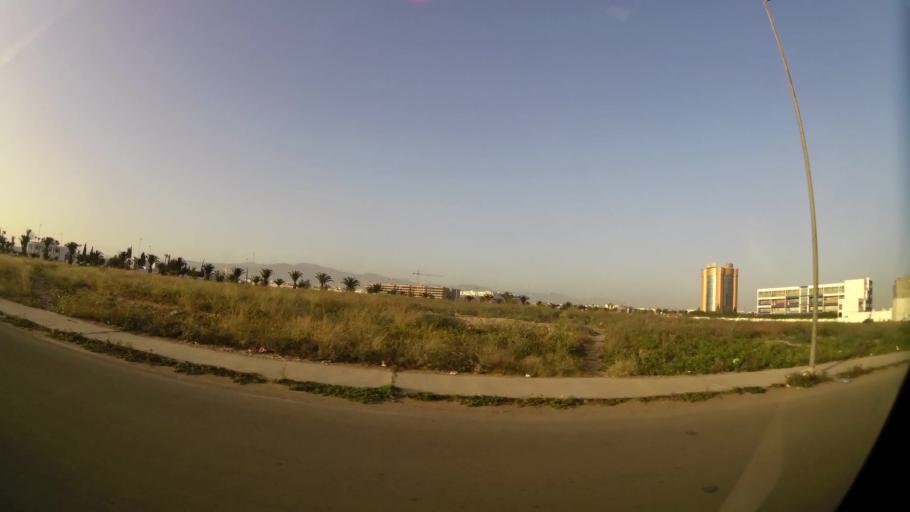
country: MA
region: Oued ed Dahab-Lagouira
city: Dakhla
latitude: 30.4020
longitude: -9.5701
